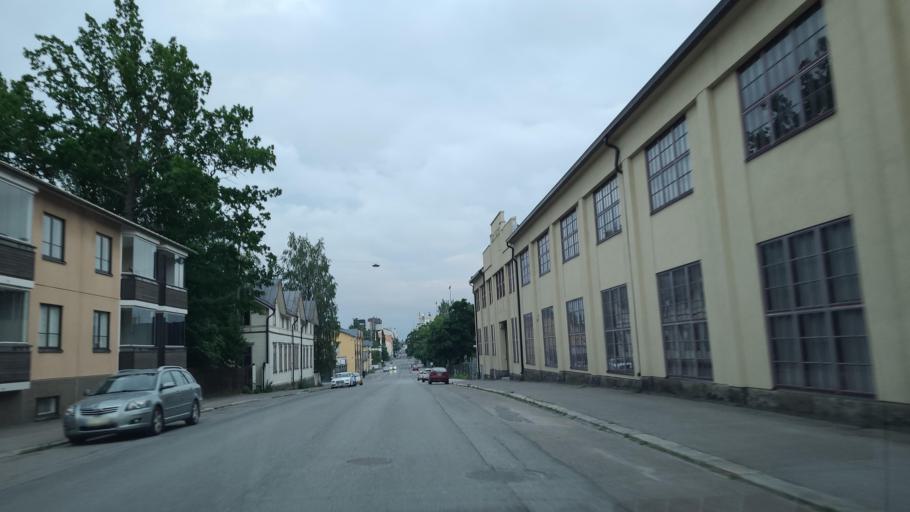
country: FI
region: Ostrobothnia
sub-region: Vaasa
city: Vaasa
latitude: 63.1025
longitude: 21.6134
